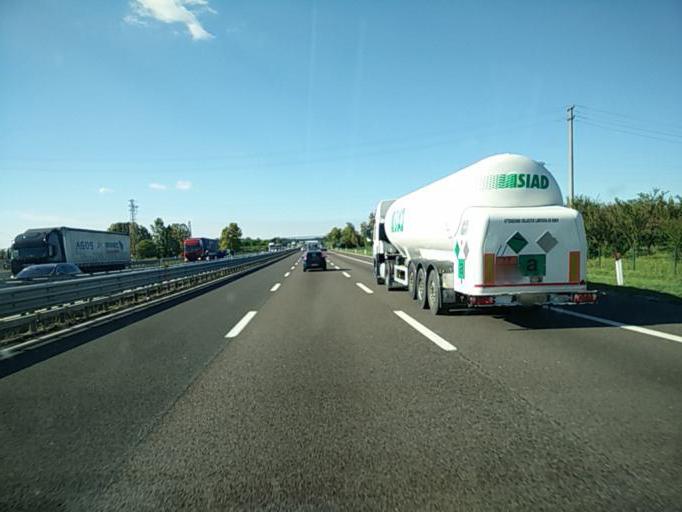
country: IT
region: Veneto
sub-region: Provincia di Verona
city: San Giorgio in Salici
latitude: 45.4167
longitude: 10.8061
